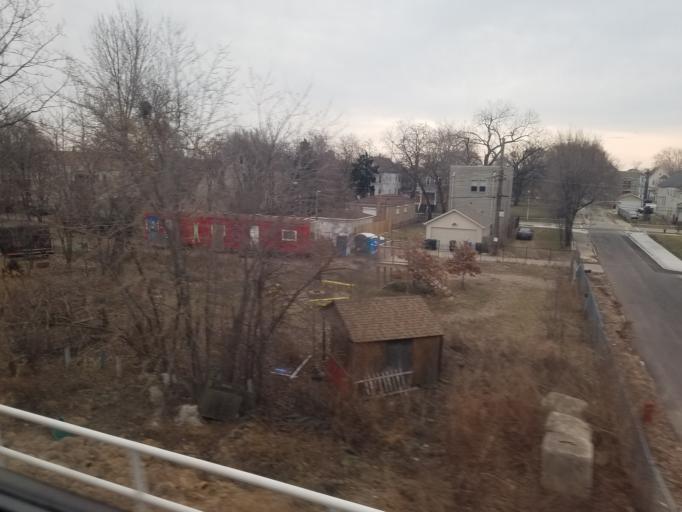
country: US
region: Illinois
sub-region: Cook County
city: Chicago
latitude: 41.8134
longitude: -87.6357
